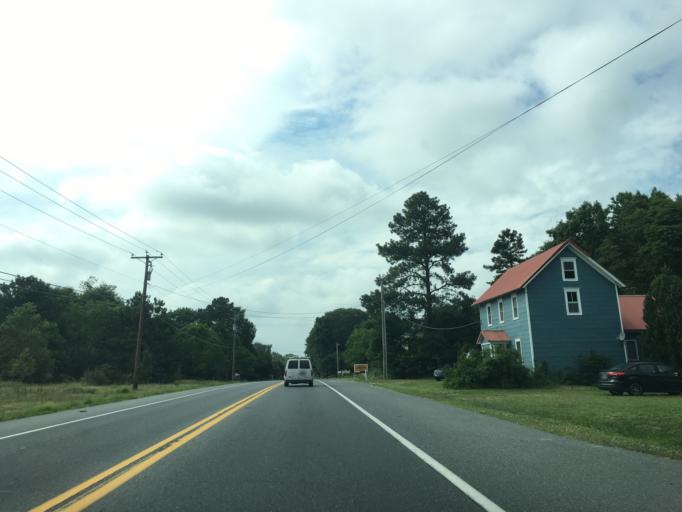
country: US
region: Delaware
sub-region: Sussex County
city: Ocean View
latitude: 38.5514
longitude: -75.1503
